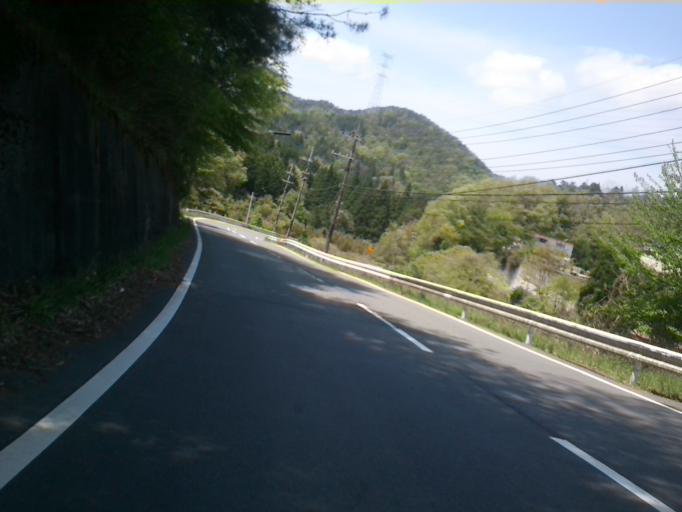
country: JP
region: Kyoto
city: Kameoka
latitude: 34.9629
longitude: 135.5321
